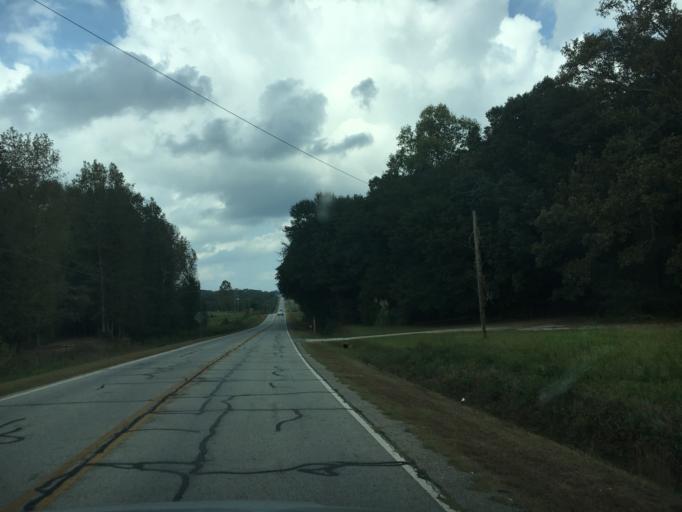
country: US
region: Georgia
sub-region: Hart County
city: Hartwell
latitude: 34.2725
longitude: -82.8991
